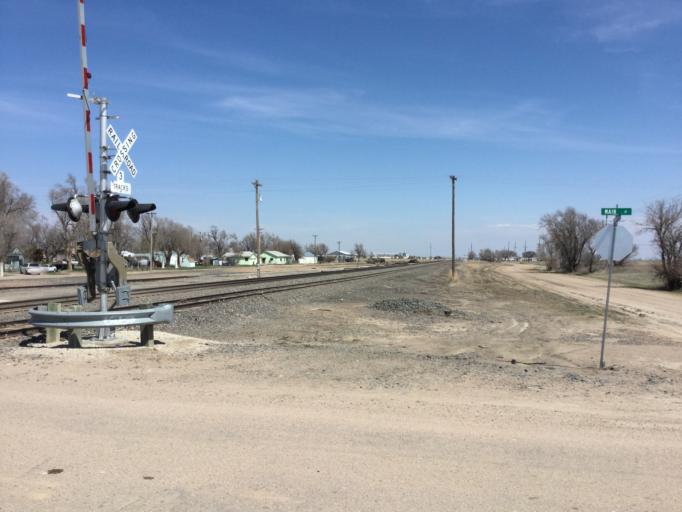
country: US
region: Kansas
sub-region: Kearny County
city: Lakin
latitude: 37.9783
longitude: -101.1326
